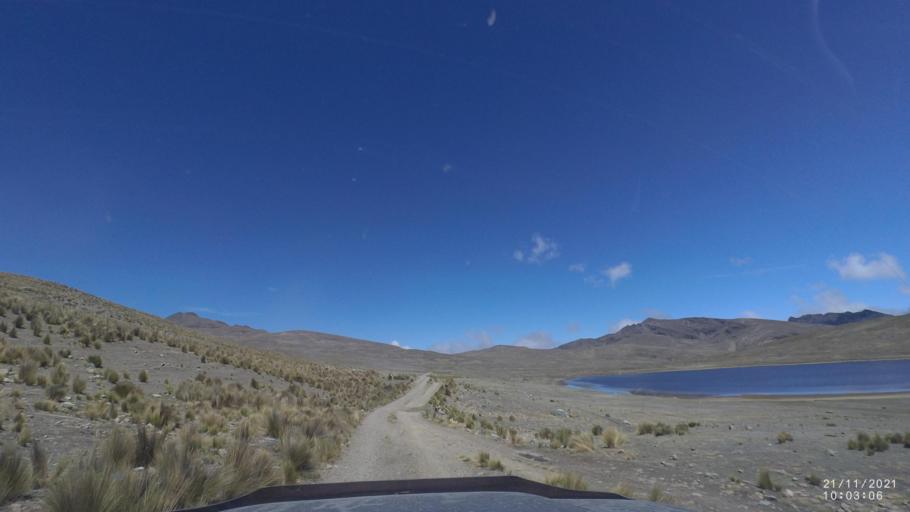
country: BO
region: Cochabamba
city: Cochabamba
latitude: -17.0279
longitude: -66.2773
